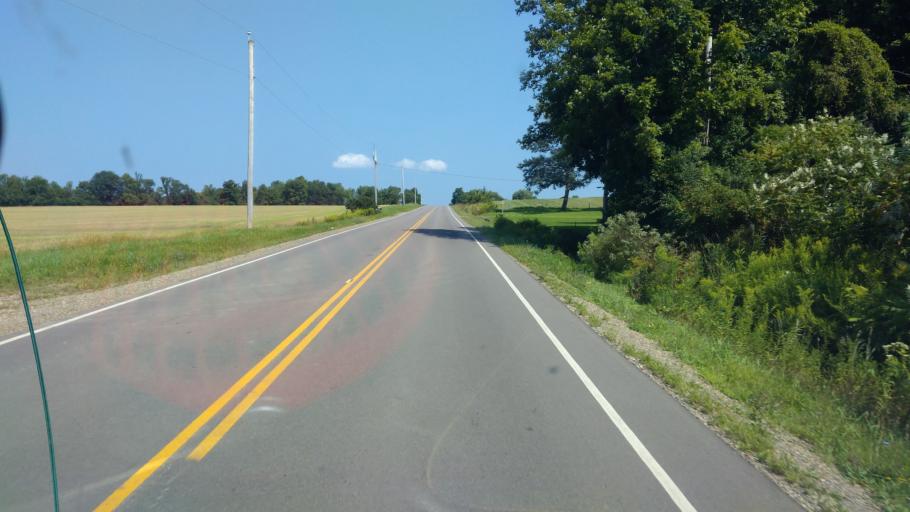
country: US
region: New York
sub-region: Allegany County
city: Belmont
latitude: 42.2508
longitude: -78.0401
